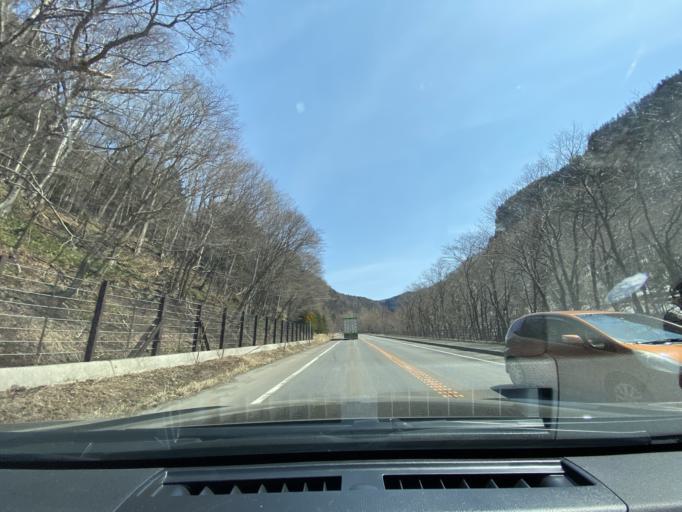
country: JP
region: Hokkaido
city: Kamikawa
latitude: 43.7261
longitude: 142.9664
